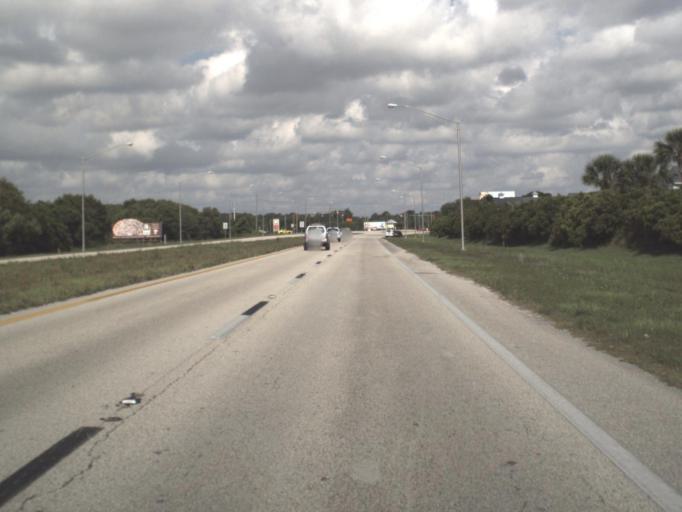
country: US
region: Florida
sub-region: Saint Johns County
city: Saint Augustine Beach
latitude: 29.8615
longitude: -81.2861
